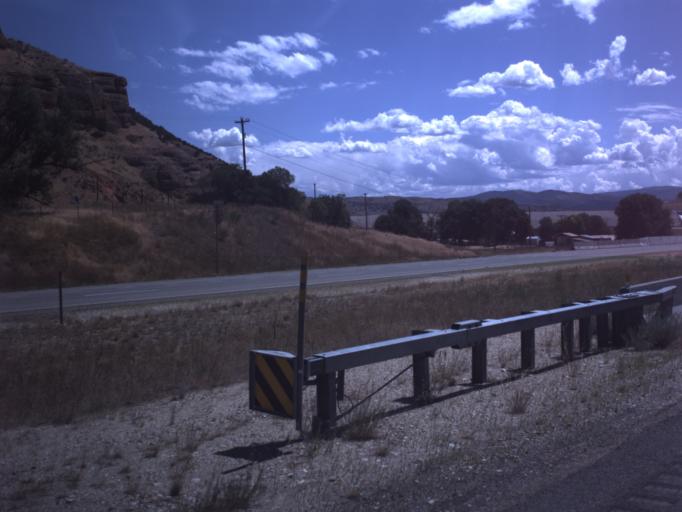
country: US
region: Utah
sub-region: Summit County
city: Coalville
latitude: 40.9739
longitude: -111.4439
